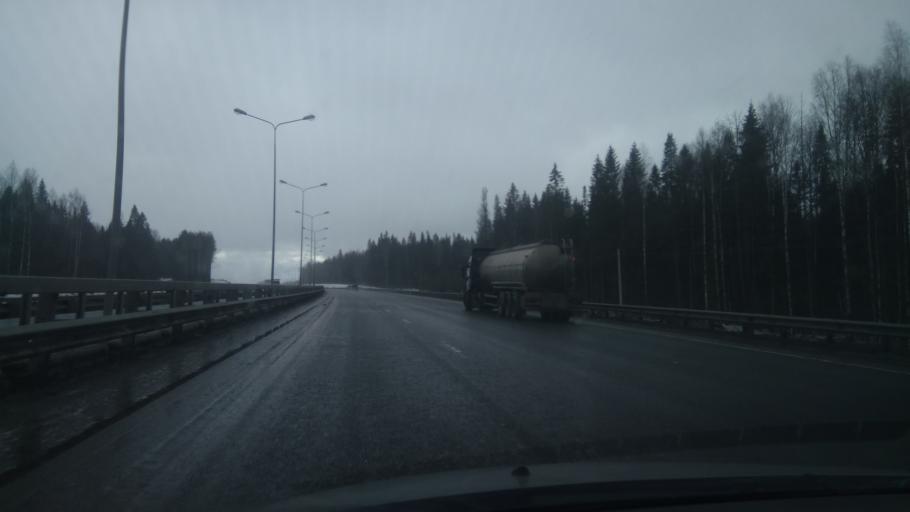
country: RU
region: Perm
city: Zvezdnyy
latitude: 57.7473
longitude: 56.3346
